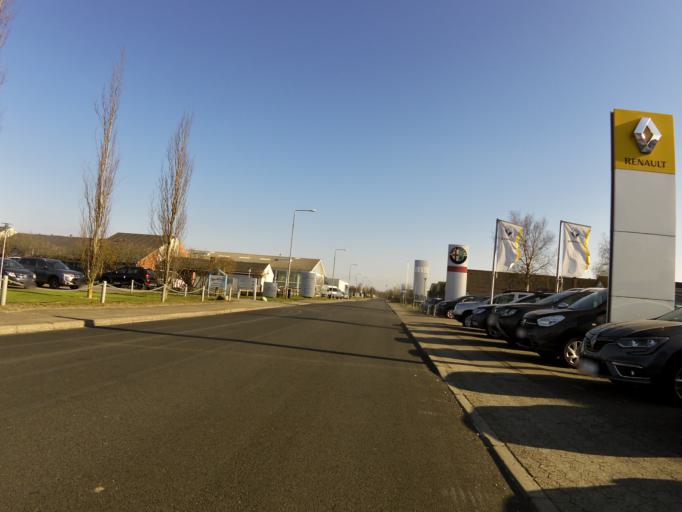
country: DK
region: South Denmark
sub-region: Esbjerg Kommune
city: Ribe
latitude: 55.3552
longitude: 8.7737
